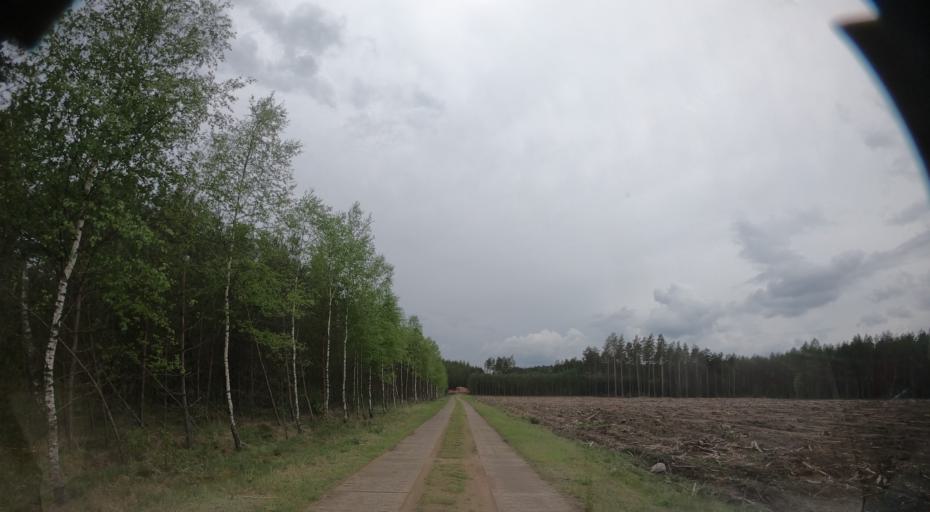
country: PL
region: West Pomeranian Voivodeship
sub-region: Powiat koszalinski
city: Bobolice
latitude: 54.0643
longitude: 16.4249
